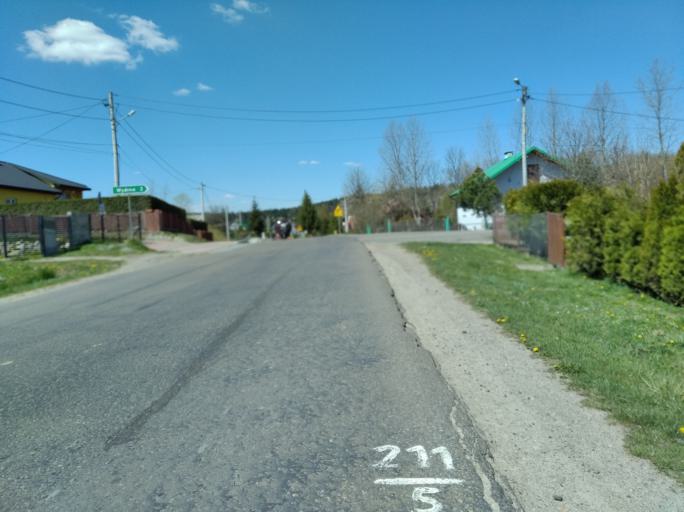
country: PL
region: Subcarpathian Voivodeship
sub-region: Powiat brzozowski
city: Dydnia
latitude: 49.6948
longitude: 22.1507
